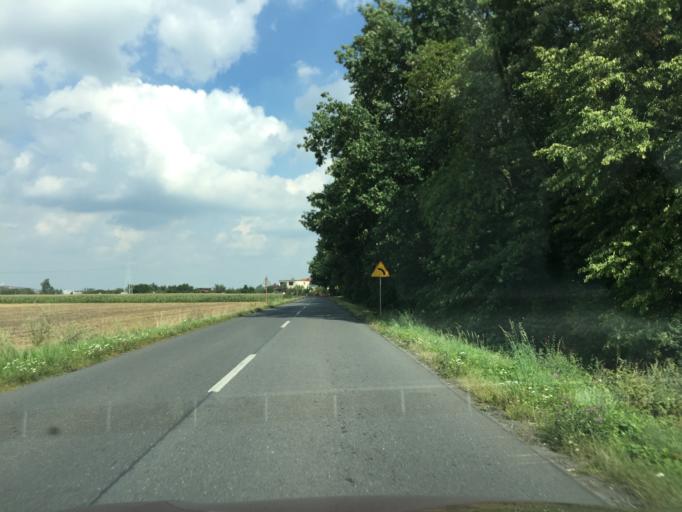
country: PL
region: Greater Poland Voivodeship
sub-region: Powiat kaliski
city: Stawiszyn
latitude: 51.9409
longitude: 18.1501
